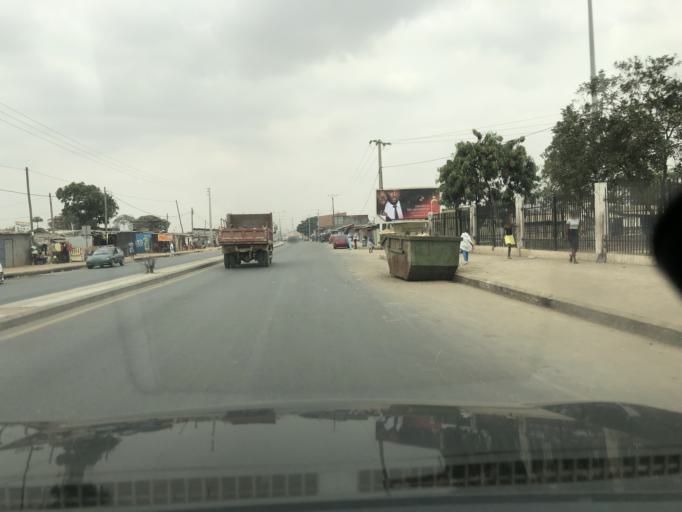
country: AO
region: Luanda
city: Luanda
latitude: -8.8299
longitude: 13.2828
